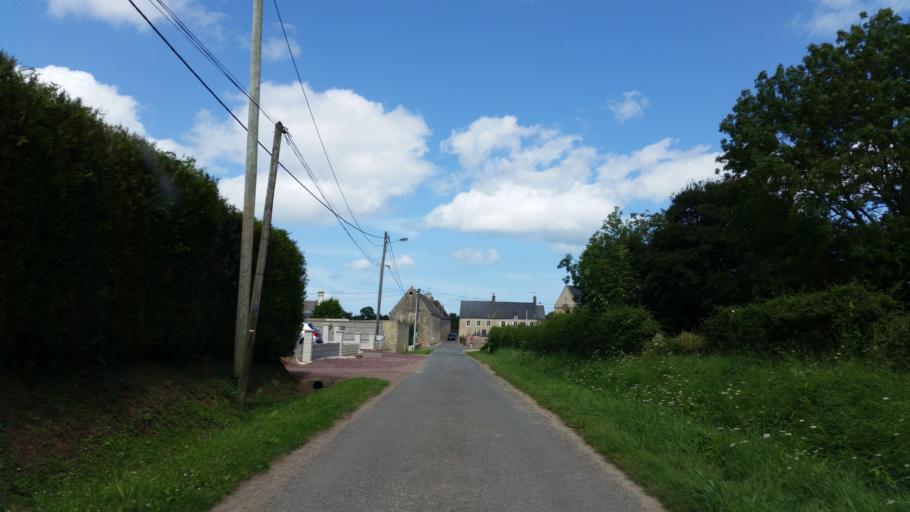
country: FR
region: Lower Normandy
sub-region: Departement de la Manche
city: Montebourg
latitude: 49.4580
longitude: -1.3436
